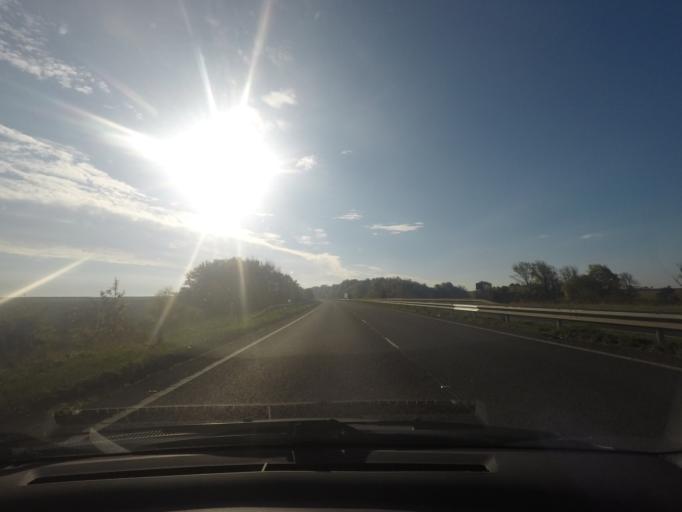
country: GB
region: England
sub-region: North Lincolnshire
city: Barton upon Humber
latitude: 53.6440
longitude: -0.4501
